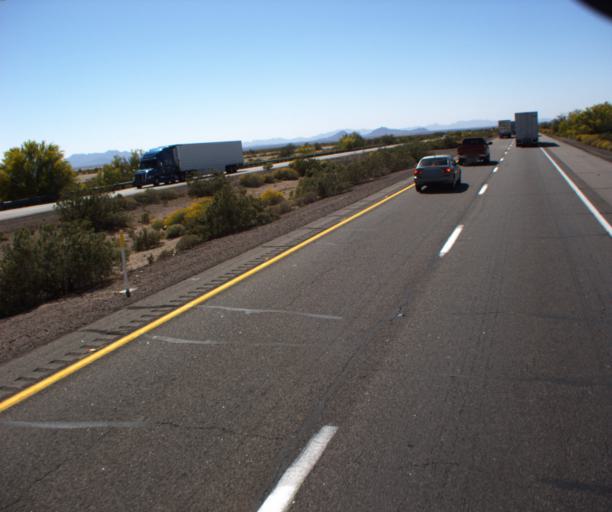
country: US
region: Arizona
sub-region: Yuma County
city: Wellton
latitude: 32.7197
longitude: -113.7822
